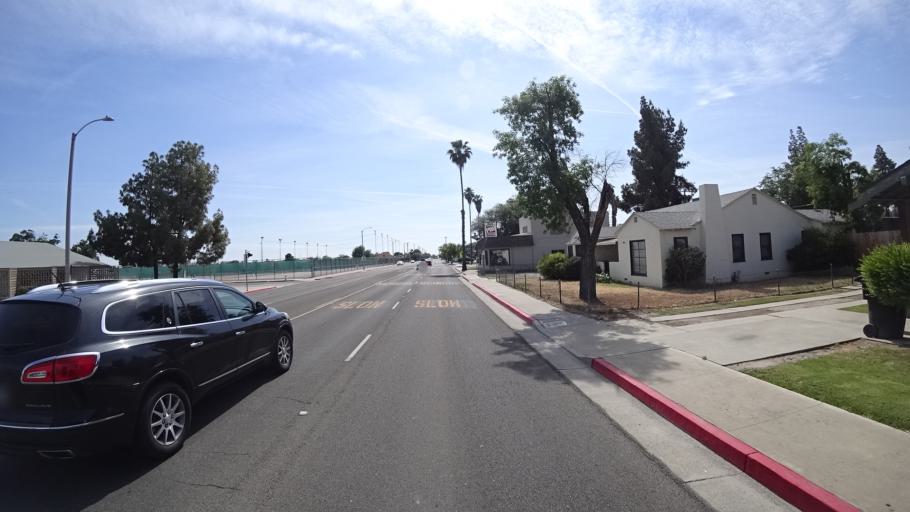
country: US
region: California
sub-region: Kings County
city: Hanford
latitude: 36.3426
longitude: -119.6438
